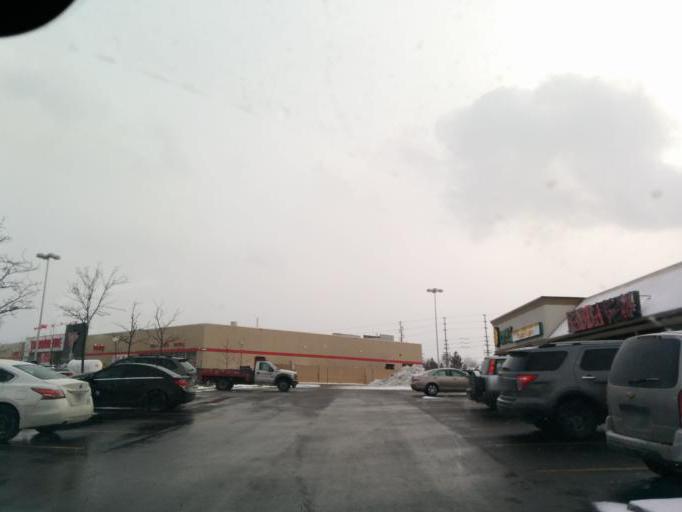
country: CA
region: Ontario
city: Brampton
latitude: 43.5832
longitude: -79.7617
